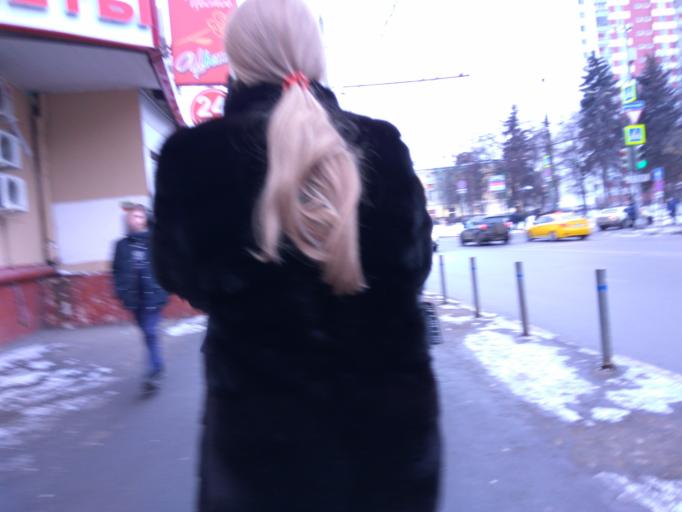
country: RU
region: Moskovskaya
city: Izmaylovo
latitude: 55.7973
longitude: 37.7994
